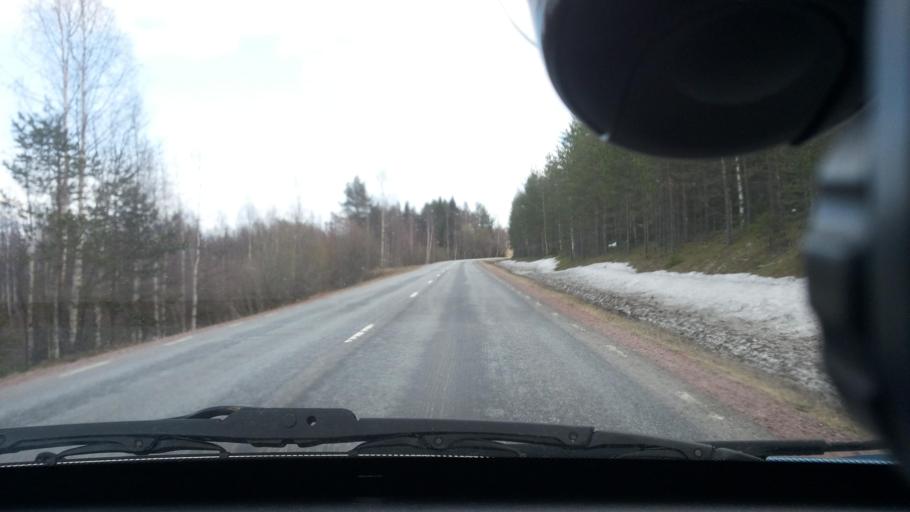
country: SE
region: Norrbotten
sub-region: Lulea Kommun
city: Sodra Sunderbyn
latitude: 65.6597
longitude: 21.8335
